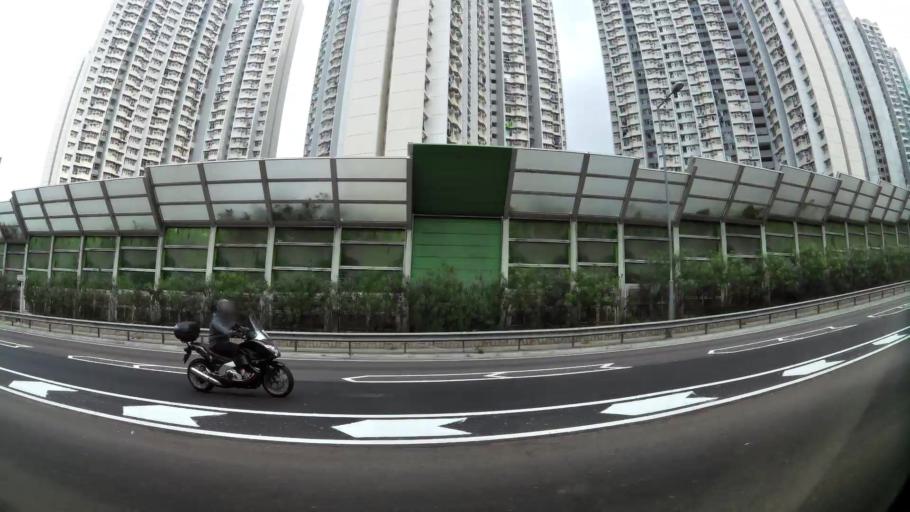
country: HK
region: Kowloon City
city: Kowloon
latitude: 22.3115
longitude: 114.2327
